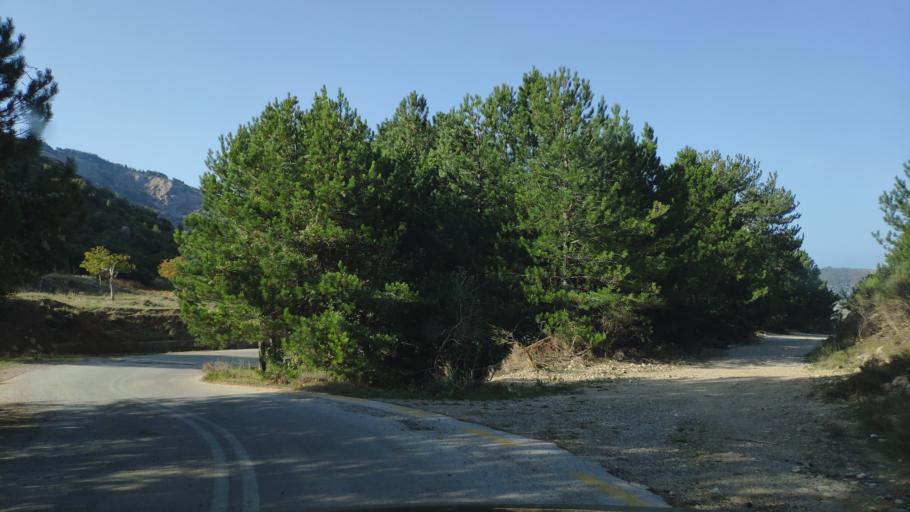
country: GR
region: West Greece
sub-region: Nomos Achaias
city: Aiyira
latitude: 38.0565
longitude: 22.3818
